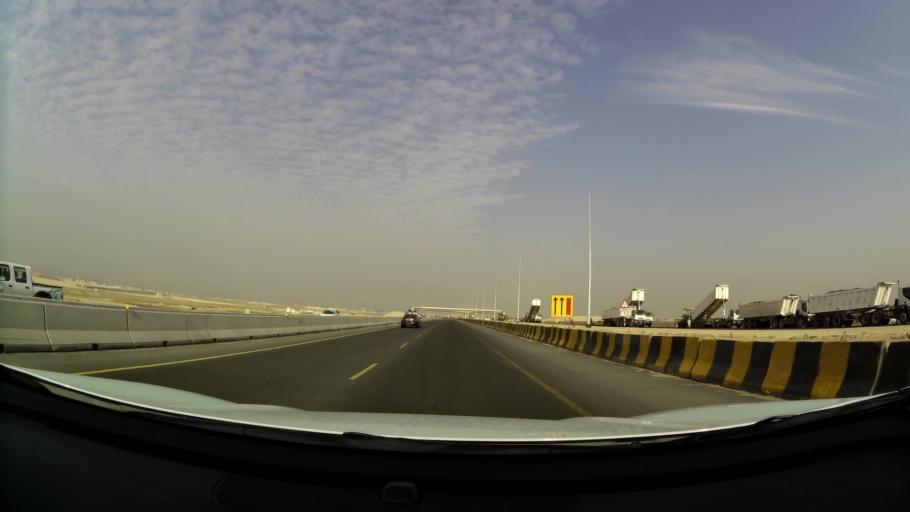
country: AE
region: Abu Dhabi
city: Abu Dhabi
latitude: 24.2765
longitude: 54.5196
